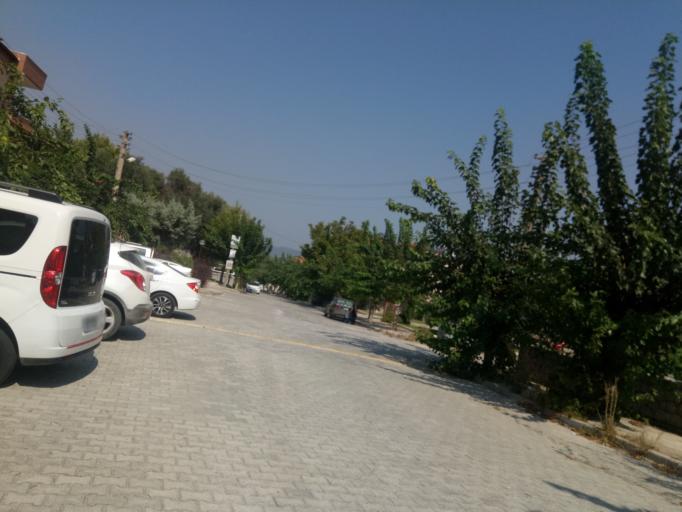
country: TR
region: Izmir
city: Urla
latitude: 38.3262
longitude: 26.7699
